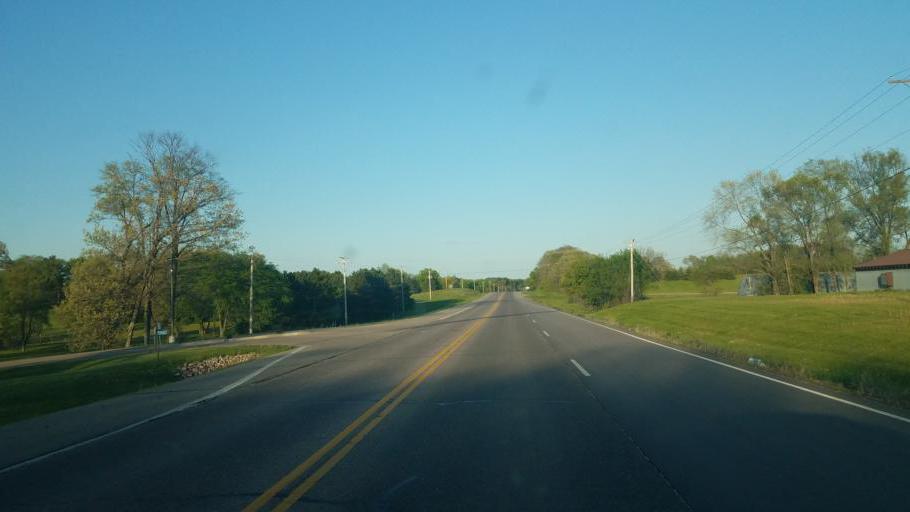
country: US
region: Wisconsin
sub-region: Sauk County
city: Reedsburg
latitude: 43.5330
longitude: -89.9433
